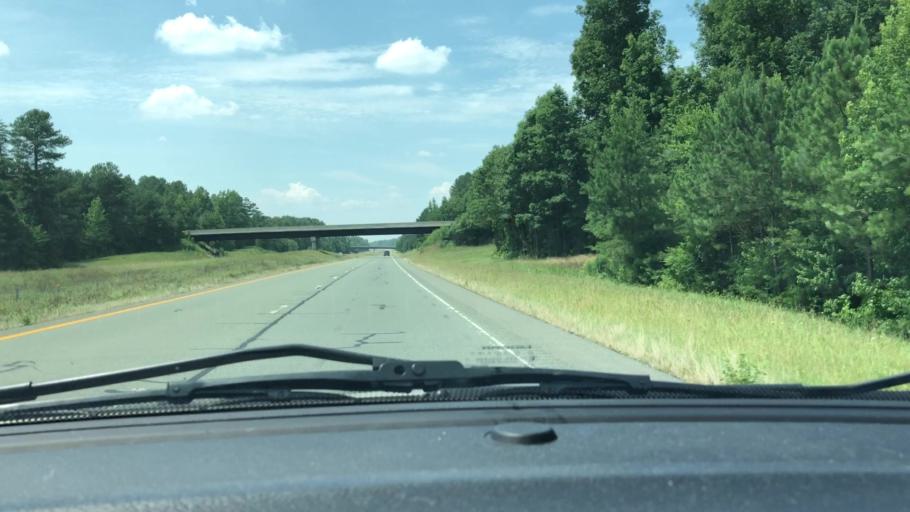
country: US
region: North Carolina
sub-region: Randolph County
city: Liberty
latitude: 35.7962
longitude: -79.5332
